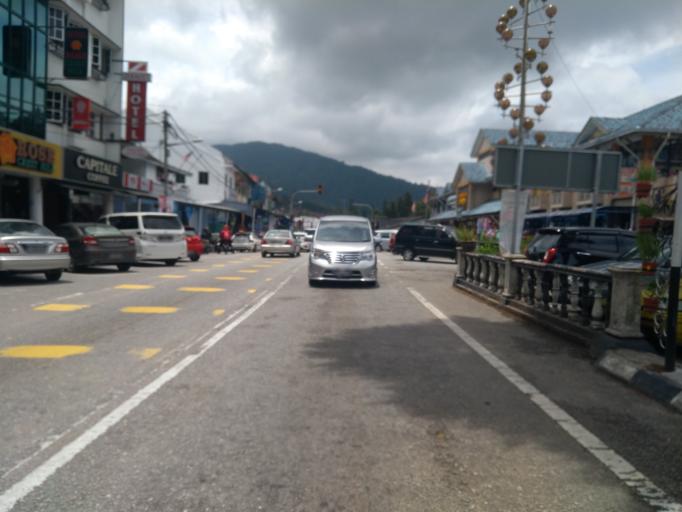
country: MY
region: Pahang
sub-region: Cameron Highlands
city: Tanah Rata
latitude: 4.4705
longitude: 101.3766
